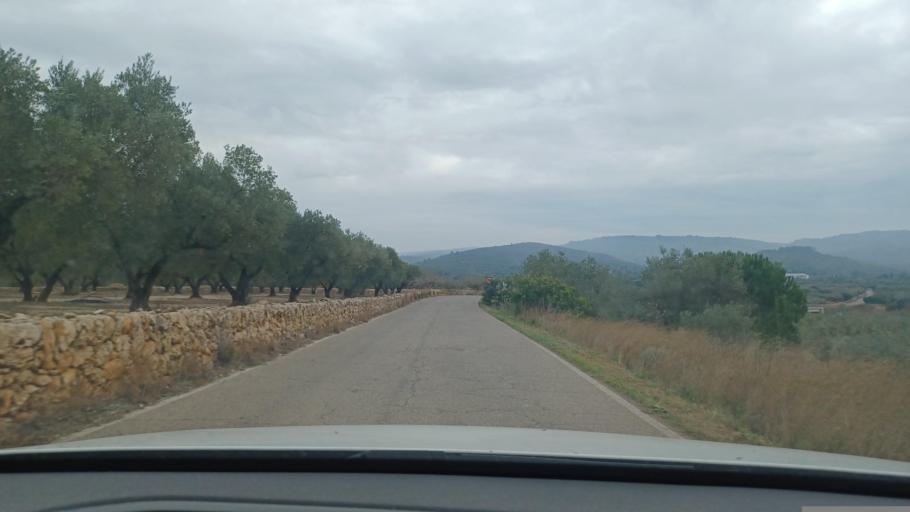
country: ES
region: Catalonia
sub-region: Provincia de Tarragona
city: Santa Barbara
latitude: 40.6666
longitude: 0.4496
